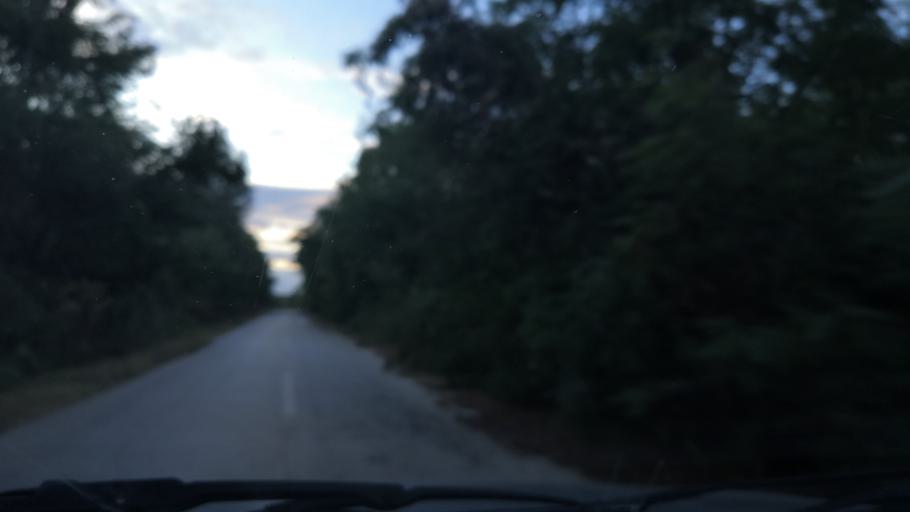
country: RO
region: Mehedinti
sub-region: Comuna Gruia
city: Izvoarele
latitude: 44.2836
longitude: 22.6376
